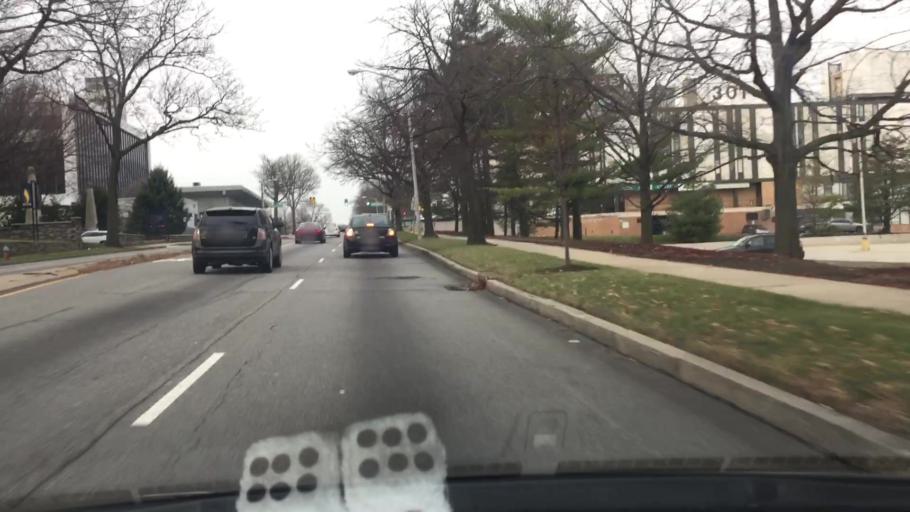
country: US
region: Pennsylvania
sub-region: Montgomery County
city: Bala-Cynwyd
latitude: 40.0059
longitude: -75.2168
